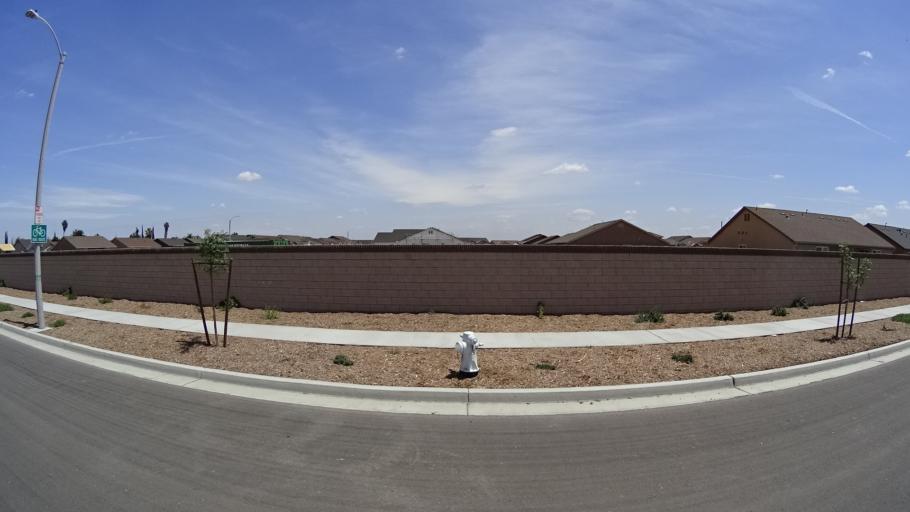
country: US
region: California
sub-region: Kings County
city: Hanford
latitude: 36.3083
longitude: -119.6729
